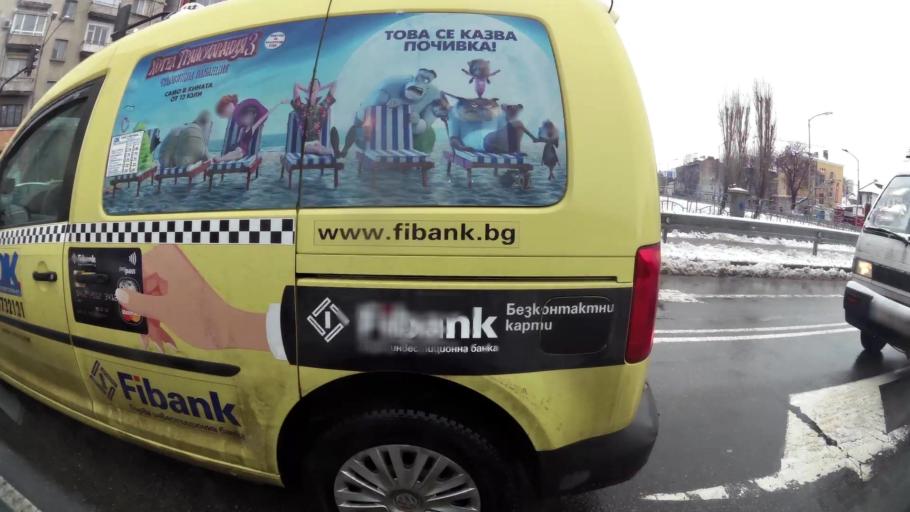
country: BG
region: Sofia-Capital
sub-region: Stolichna Obshtina
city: Sofia
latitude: 42.7045
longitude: 23.3288
